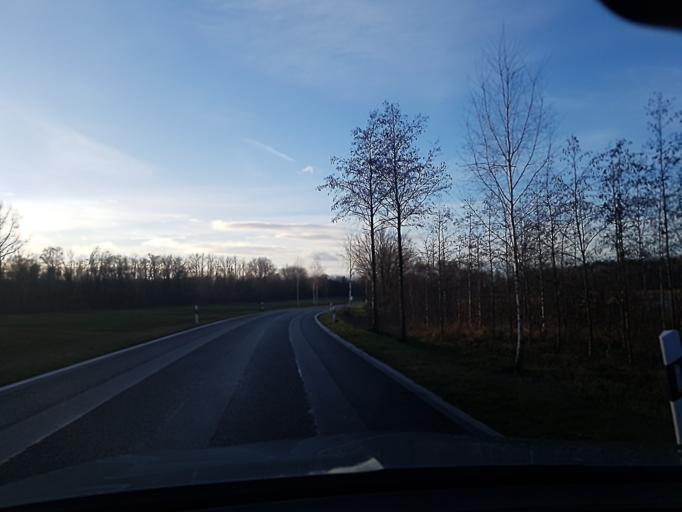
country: DE
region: Brandenburg
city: Trobitz
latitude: 51.5916
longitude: 13.4223
